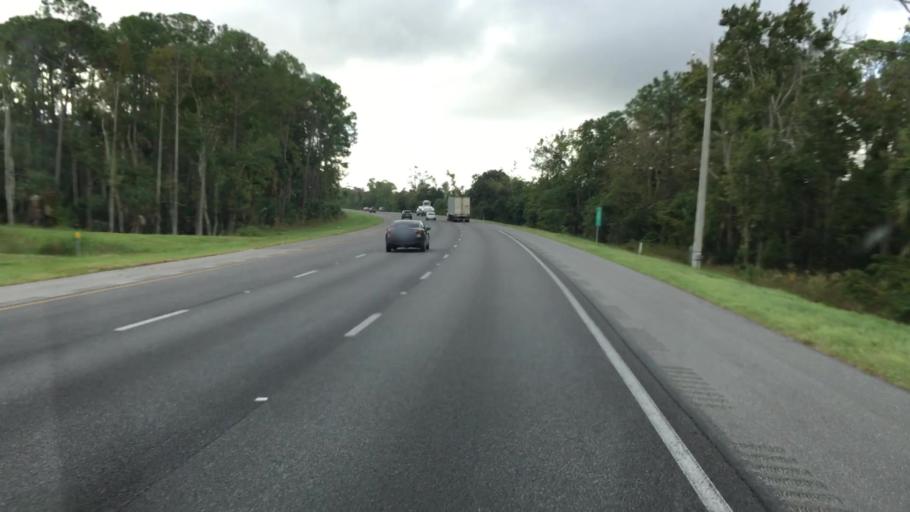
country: US
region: Florida
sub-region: Volusia County
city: Glencoe
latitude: 29.0417
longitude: -81.0066
